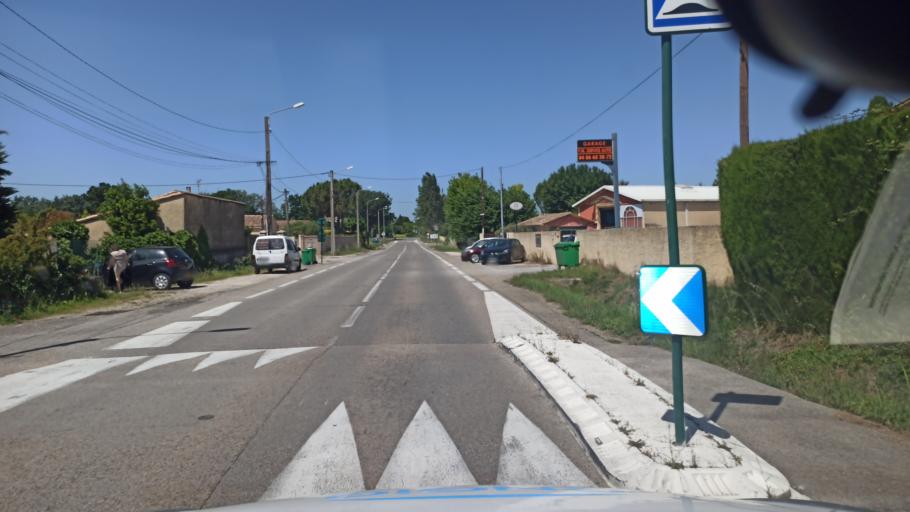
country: FR
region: Provence-Alpes-Cote d'Azur
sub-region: Departement du Vaucluse
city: Morieres-les-Avignon
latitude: 43.9494
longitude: 4.8918
